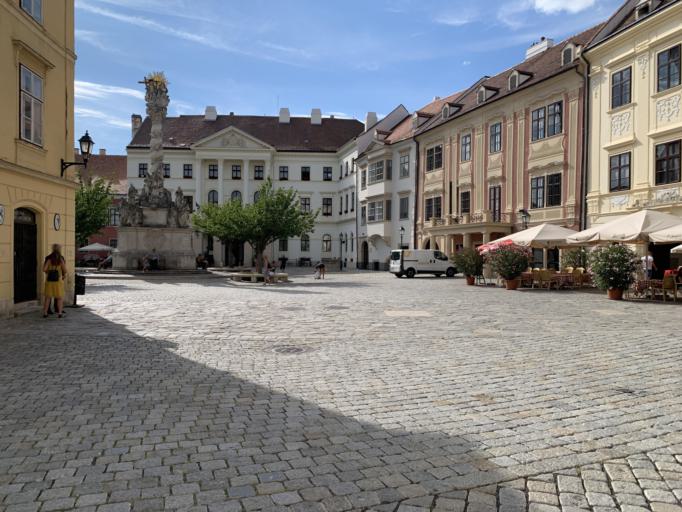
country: HU
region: Gyor-Moson-Sopron
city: Sopron
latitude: 47.6864
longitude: 16.5913
